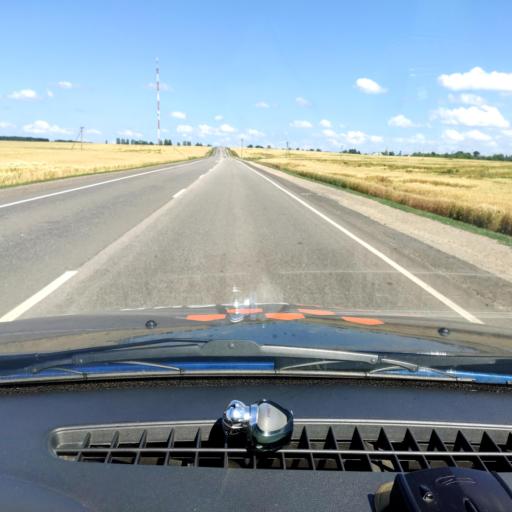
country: RU
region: Orjol
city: Livny
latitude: 52.4479
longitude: 37.4795
